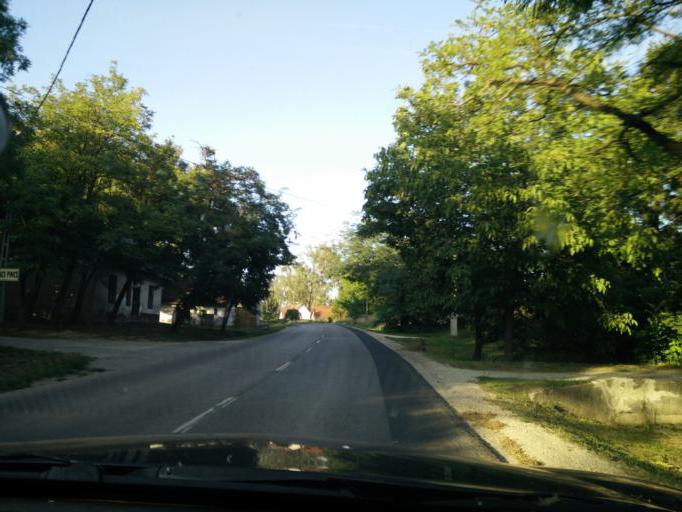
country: HU
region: Pest
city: Zsambek
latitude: 47.5717
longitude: 18.7359
